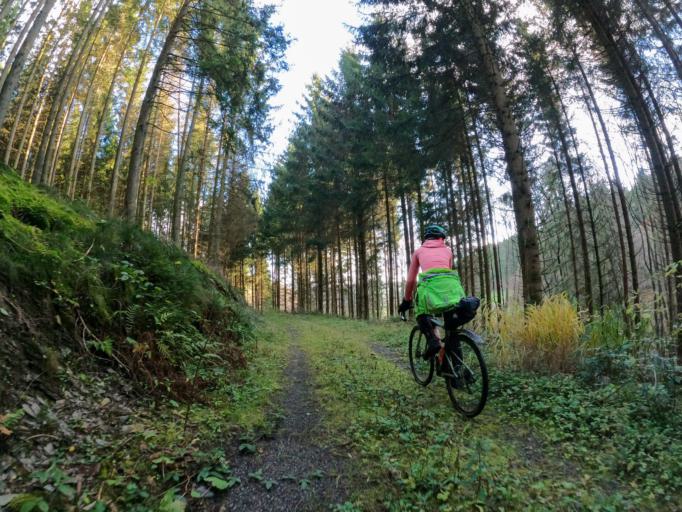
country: LU
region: Diekirch
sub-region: Canton de Wiltz
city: Bavigne
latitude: 49.9715
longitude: 5.8198
